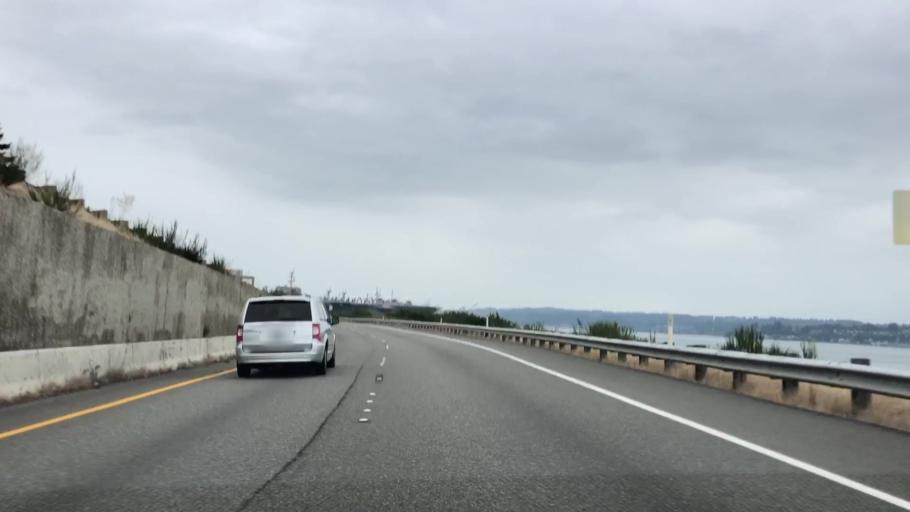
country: US
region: Washington
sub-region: Kitsap County
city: Navy Yard City
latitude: 47.5483
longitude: -122.6695
